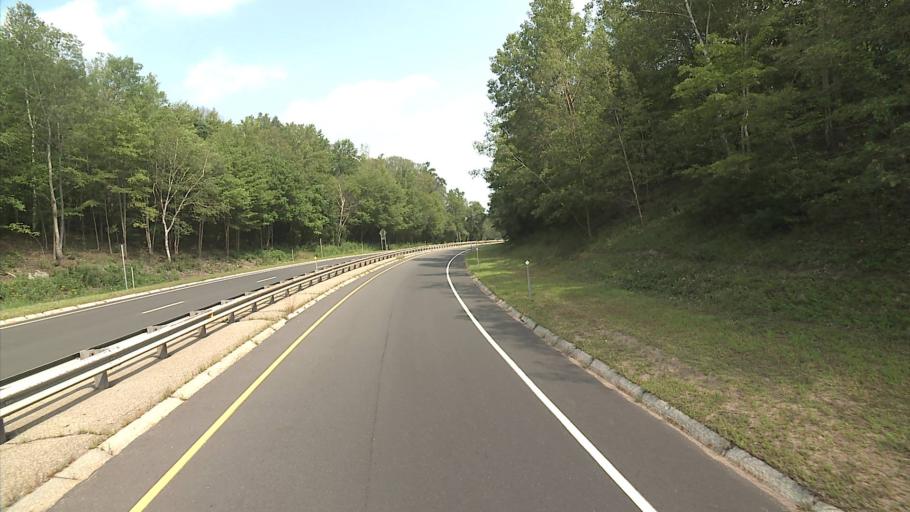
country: US
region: Connecticut
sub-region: Middlesex County
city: Chester Center
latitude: 41.4172
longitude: -72.4940
